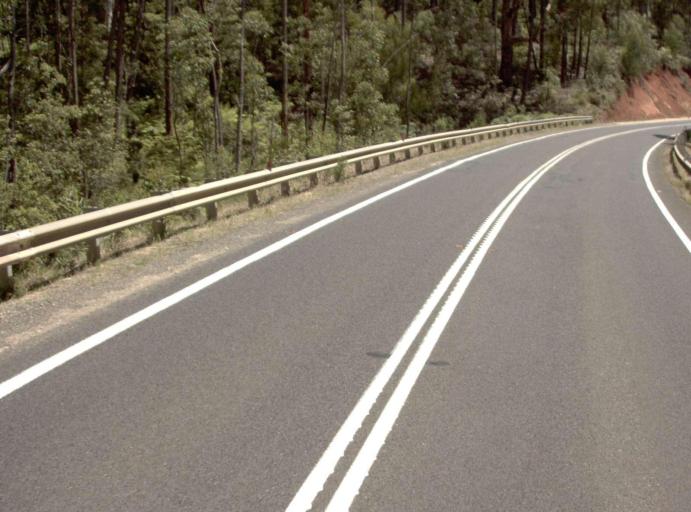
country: AU
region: New South Wales
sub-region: Bombala
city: Bombala
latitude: -37.5841
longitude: 149.0019
